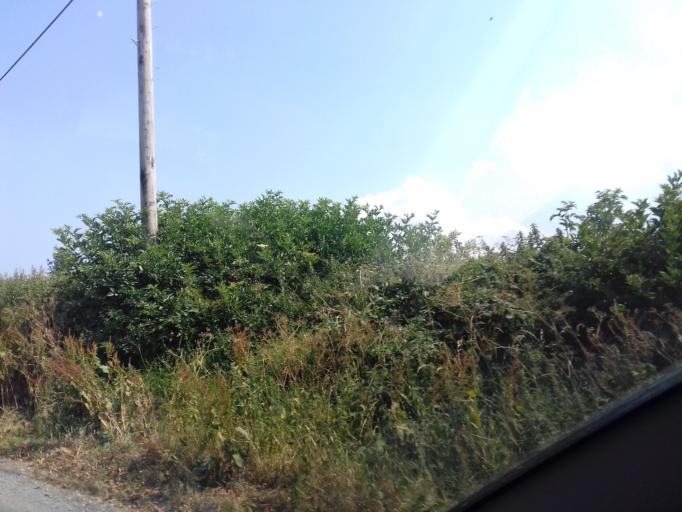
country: IE
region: Leinster
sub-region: An Mhi
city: Stamullin
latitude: 53.5959
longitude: -6.3217
